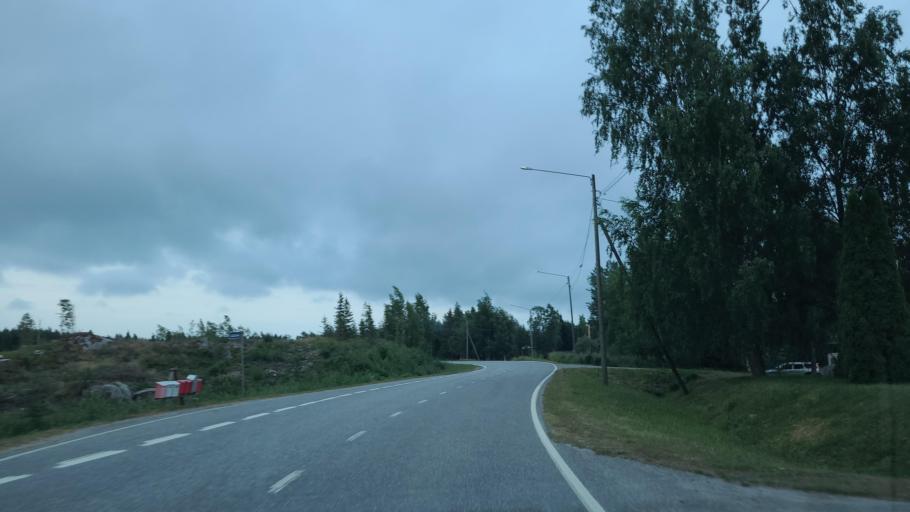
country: FI
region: Ostrobothnia
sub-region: Vaasa
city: Replot
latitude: 63.2830
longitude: 21.1259
